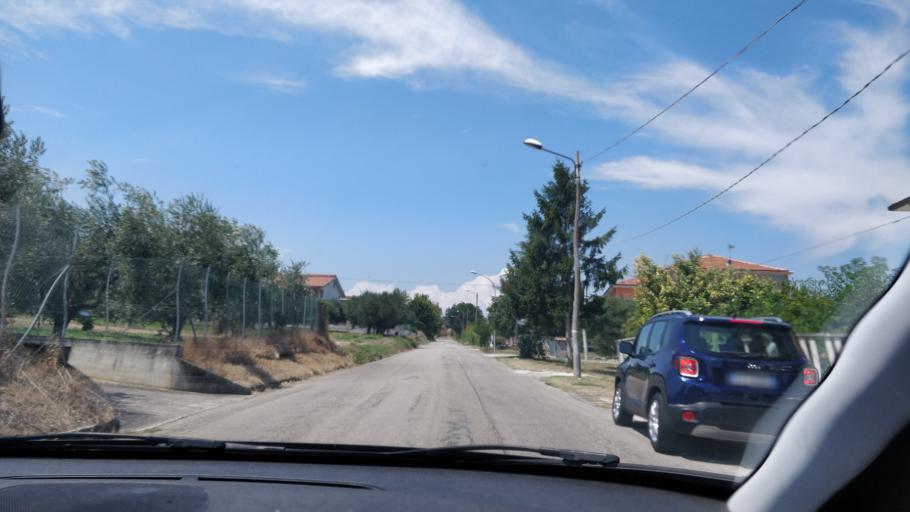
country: IT
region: Abruzzo
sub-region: Provincia di Chieti
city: Francavilla al Mare
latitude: 42.4234
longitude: 14.2607
